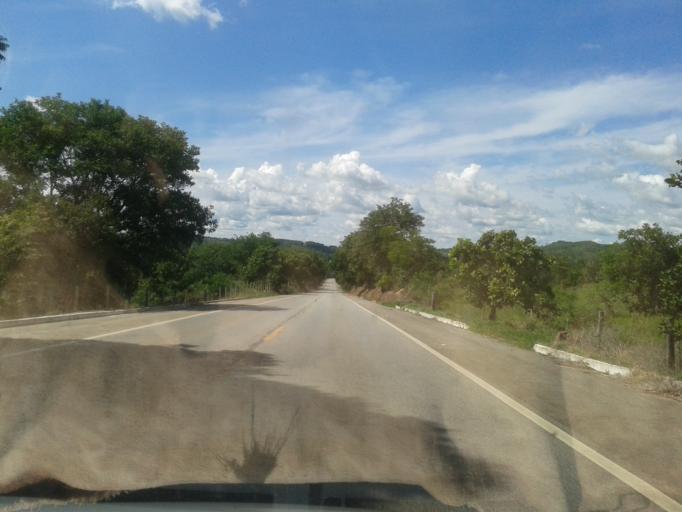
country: BR
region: Goias
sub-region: Goias
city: Goias
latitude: -15.7118
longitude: -50.1914
